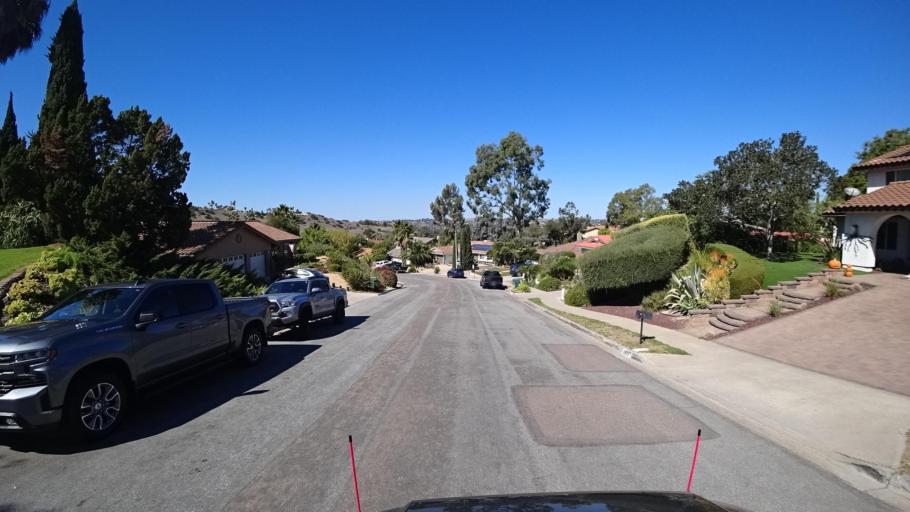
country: US
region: California
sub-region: San Diego County
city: Bonita
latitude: 32.6639
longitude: -116.9994
